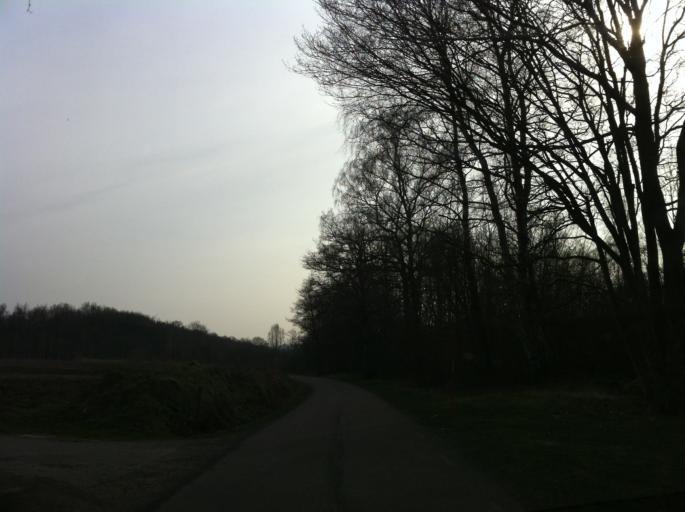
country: SE
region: Skane
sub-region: Eslovs Kommun
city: Stehag
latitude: 56.0143
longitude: 13.3968
